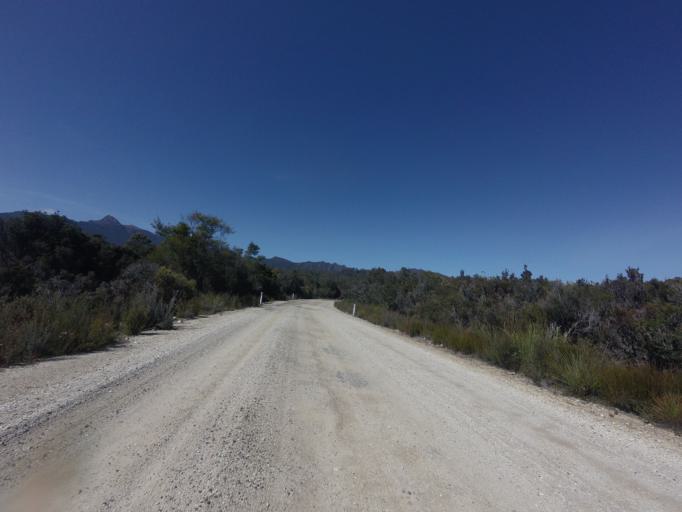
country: AU
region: Tasmania
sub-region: Huon Valley
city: Geeveston
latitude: -42.8984
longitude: 146.3744
